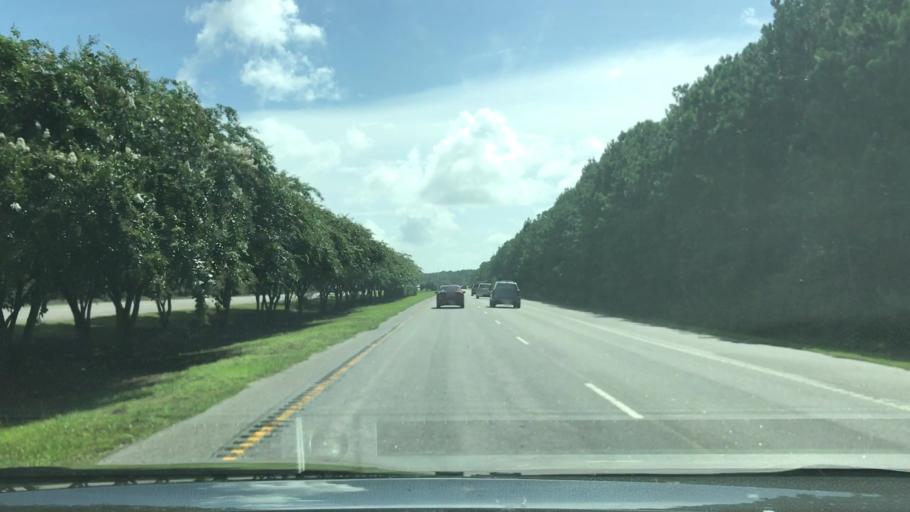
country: US
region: South Carolina
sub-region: Beaufort County
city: Hilton Head Island
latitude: 32.2009
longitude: -80.7532
